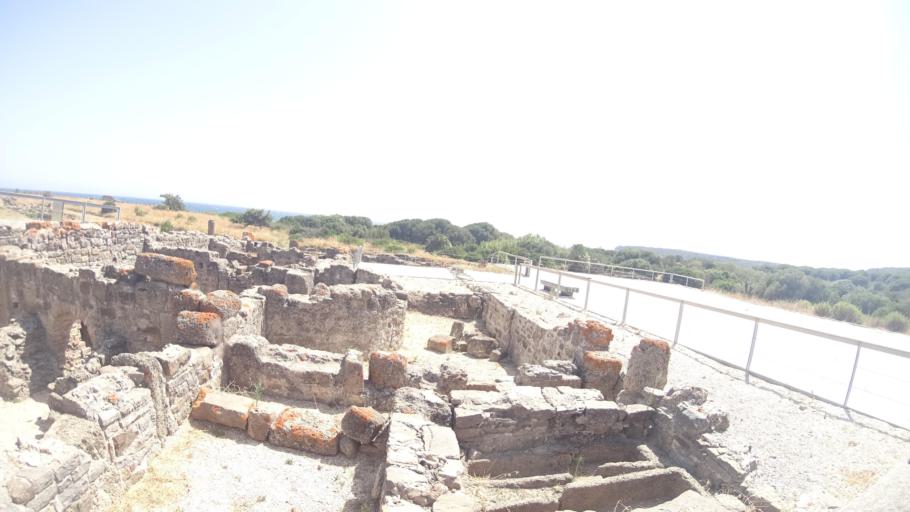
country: ES
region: Andalusia
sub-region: Provincia de Cadiz
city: Zahara de los Atunes
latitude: 36.0899
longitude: -5.7761
